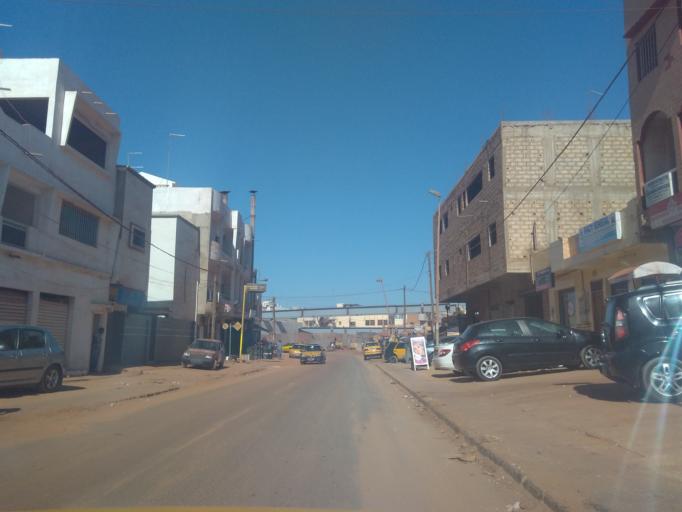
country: SN
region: Dakar
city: Grand Dakar
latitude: 14.7595
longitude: -17.4529
